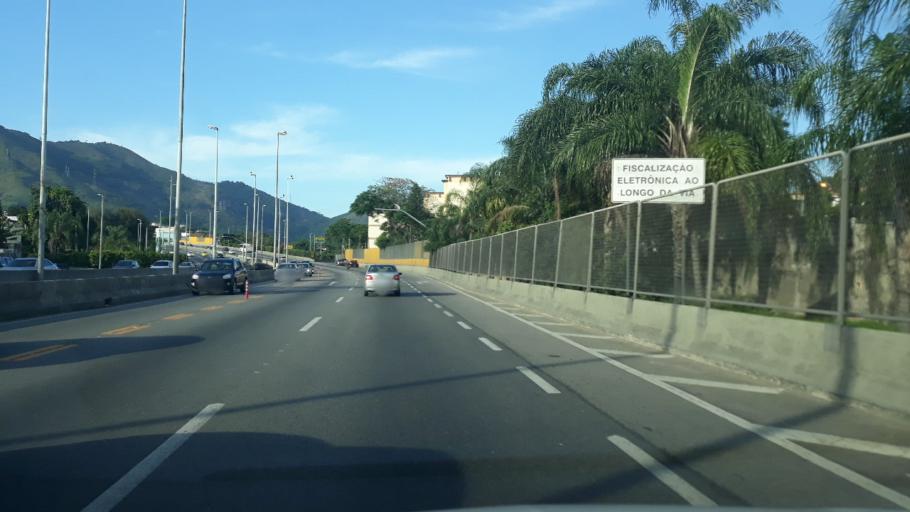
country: BR
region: Rio de Janeiro
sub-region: Rio De Janeiro
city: Rio de Janeiro
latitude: -22.8912
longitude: -43.2981
